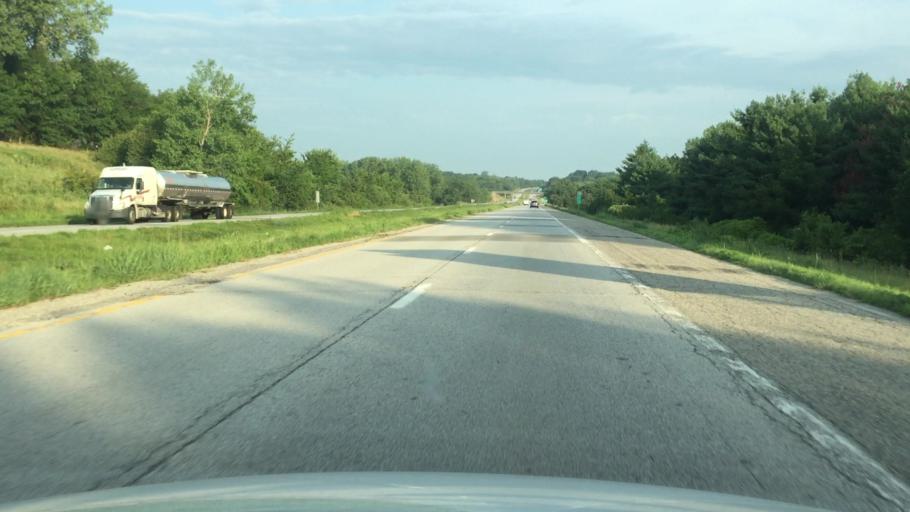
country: US
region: Missouri
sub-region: Buchanan County
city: Saint Joseph
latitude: 39.7134
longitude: -94.8082
